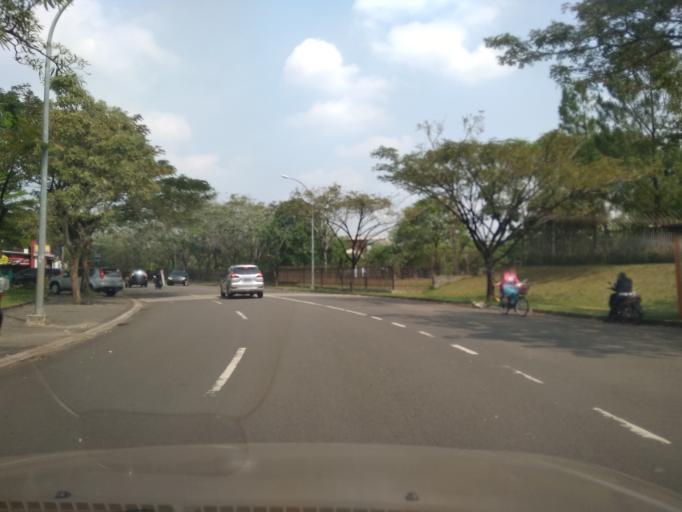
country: ID
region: West Java
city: Serpong
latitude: -6.3135
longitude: 106.6490
